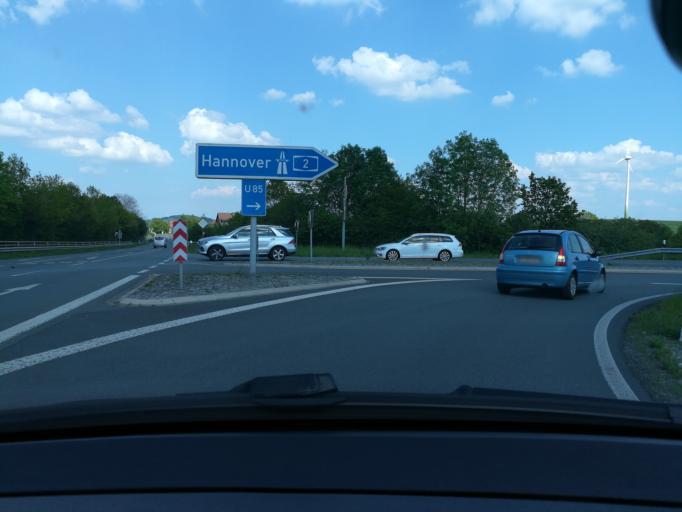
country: DE
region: North Rhine-Westphalia
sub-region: Regierungsbezirk Detmold
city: Bad Salzuflen
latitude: 52.1316
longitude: 8.7388
